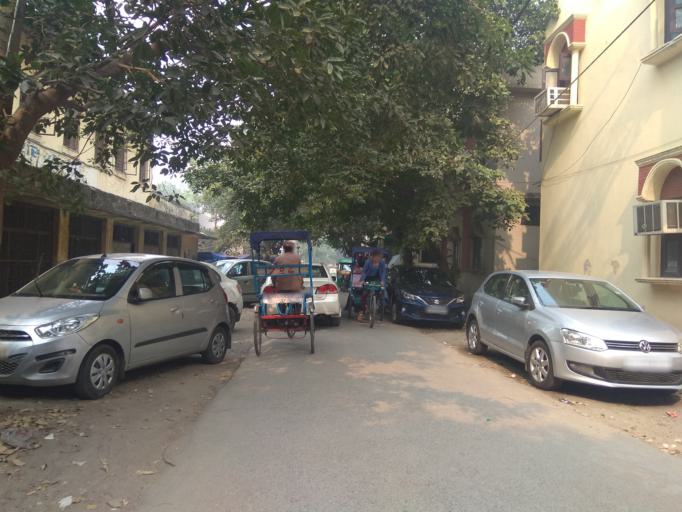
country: IN
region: NCT
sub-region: New Delhi
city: New Delhi
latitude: 28.5711
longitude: 77.2447
